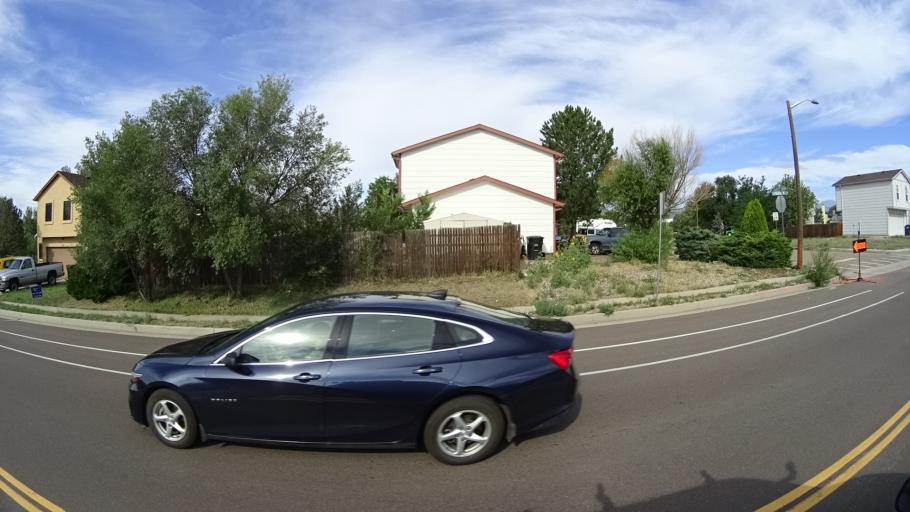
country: US
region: Colorado
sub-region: El Paso County
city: Fountain
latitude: 38.6898
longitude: -104.6935
